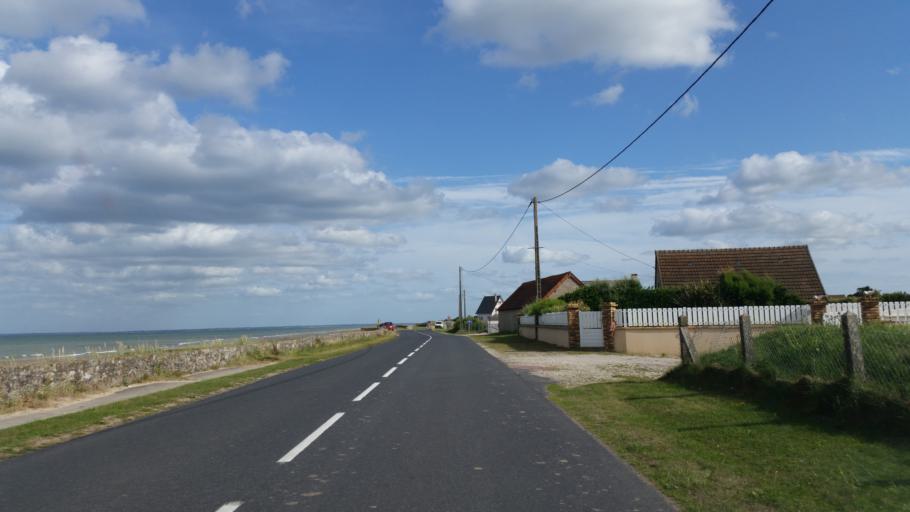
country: FR
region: Lower Normandy
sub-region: Departement de la Manche
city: Sainte-Mere-Eglise
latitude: 49.4552
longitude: -1.2225
